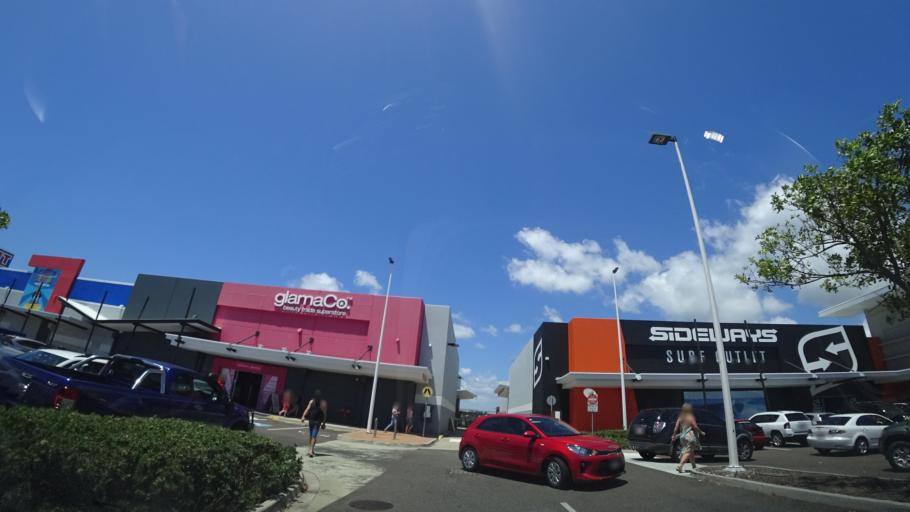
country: AU
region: Queensland
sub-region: Sunshine Coast
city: Dicky Beach
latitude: -26.7373
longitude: 153.1189
